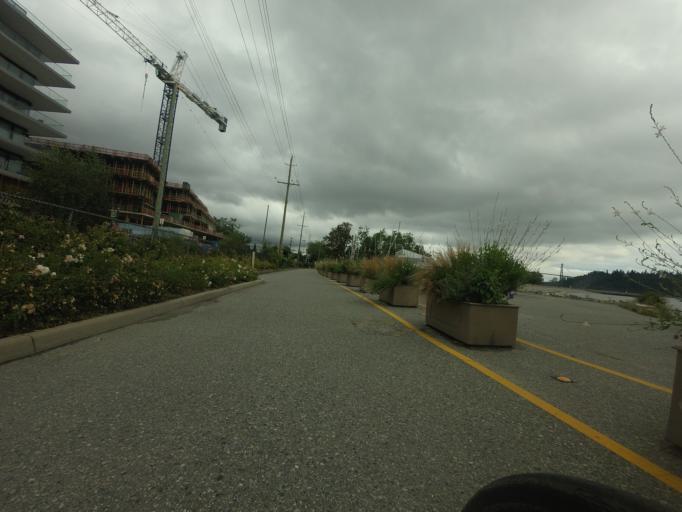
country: CA
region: British Columbia
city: West Vancouver
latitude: 49.3270
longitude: -123.1537
